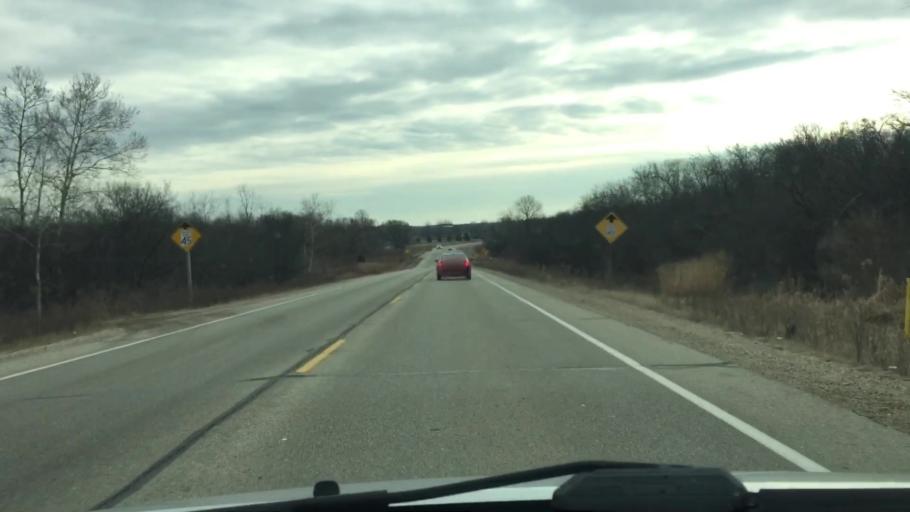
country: US
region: Wisconsin
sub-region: Walworth County
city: Elkhorn
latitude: 42.7364
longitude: -88.5474
